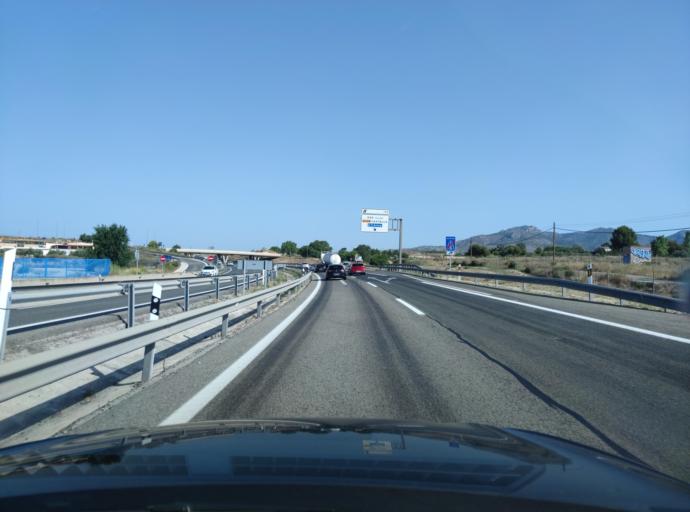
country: ES
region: Valencia
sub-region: Provincia de Alicante
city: Sax
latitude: 38.5463
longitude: -0.8138
